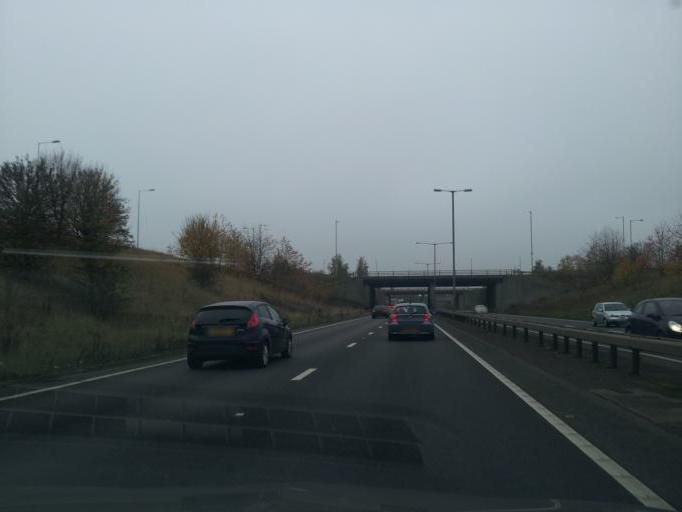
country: GB
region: England
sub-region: Leicestershire
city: Kirby Muxloe
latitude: 52.6453
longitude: -1.2228
